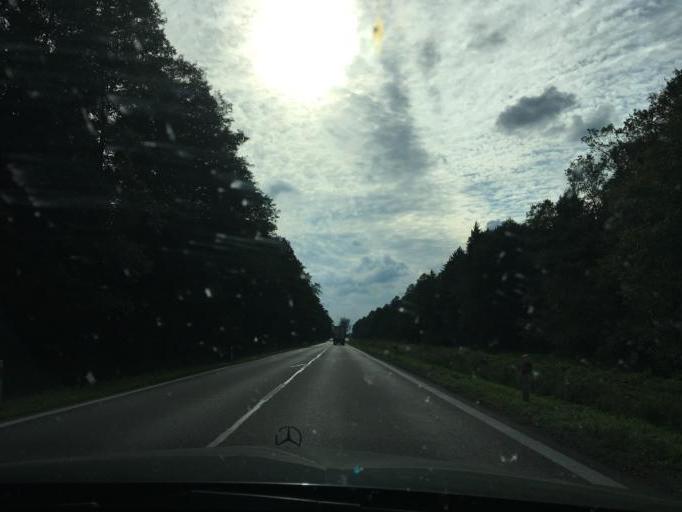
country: PL
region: Podlasie
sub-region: Powiat grajewski
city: Rajgrod
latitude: 53.6926
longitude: 22.6383
